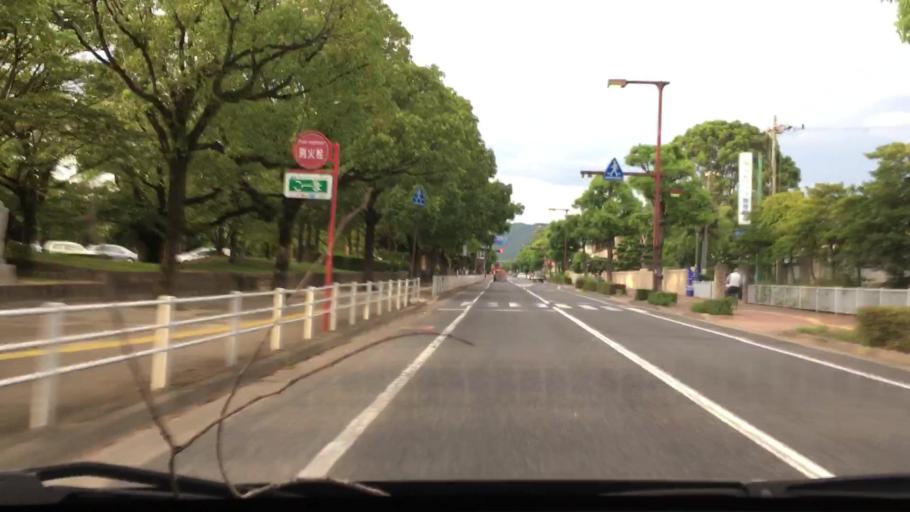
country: JP
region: Hyogo
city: Himeji
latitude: 34.8366
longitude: 134.6967
